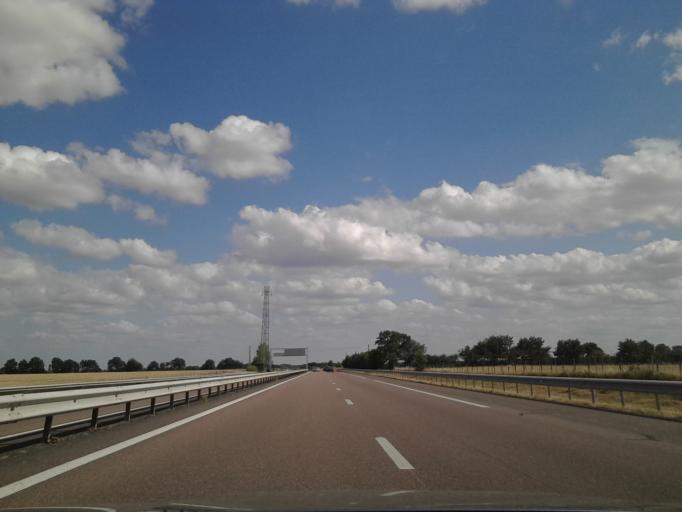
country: FR
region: Auvergne
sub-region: Departement de l'Allier
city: Estivareilles
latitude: 46.4856
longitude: 2.6658
